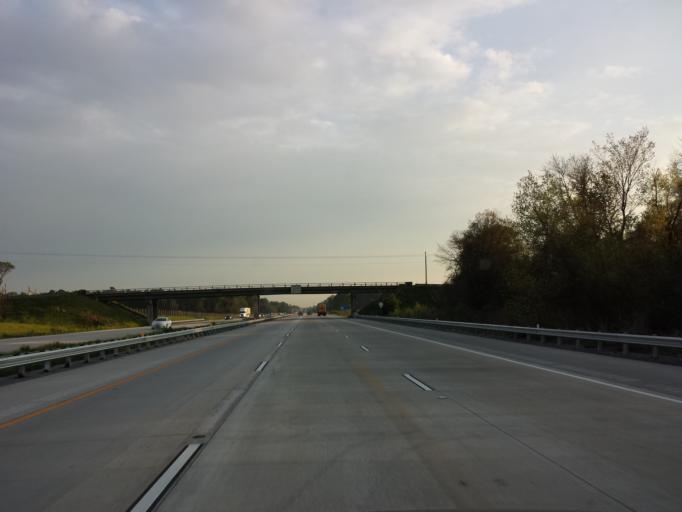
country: US
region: Georgia
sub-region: Dooly County
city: Vienna
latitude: 32.1452
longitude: -83.7572
